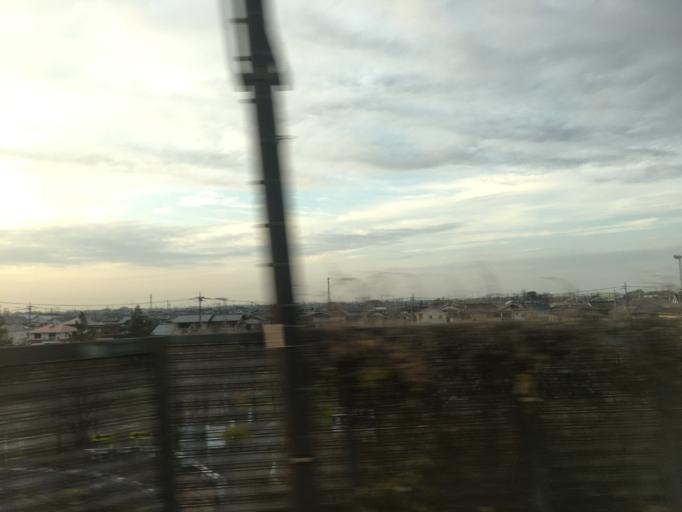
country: JP
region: Saitama
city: Kurihashi
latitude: 36.1443
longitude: 139.6958
